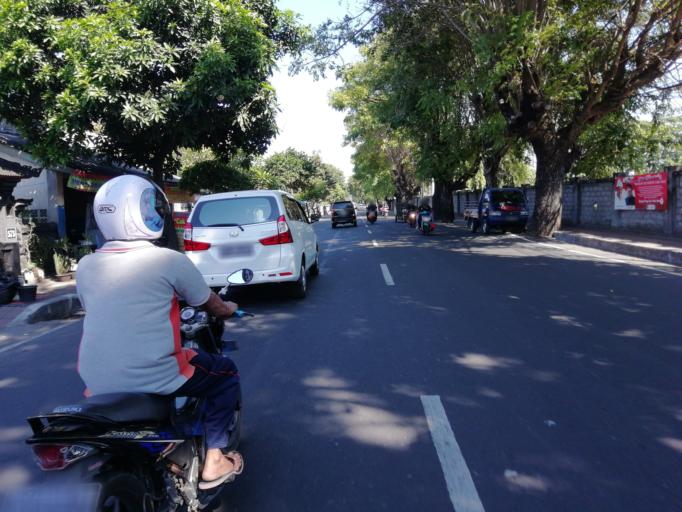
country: ID
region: Bali
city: Karyadharma
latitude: -8.7046
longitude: 115.2199
